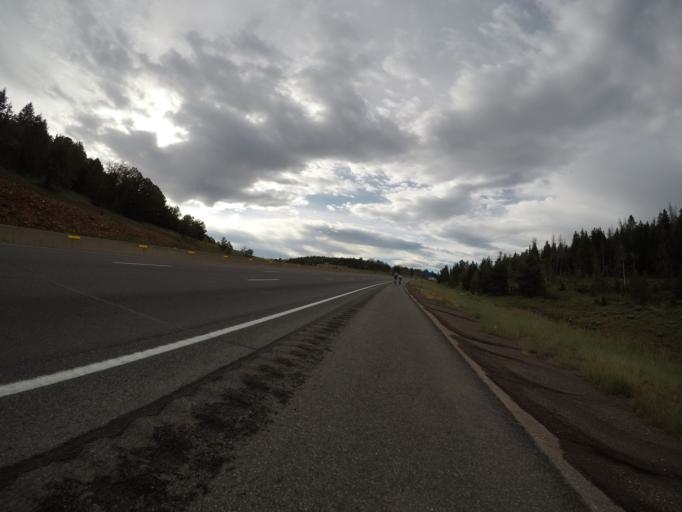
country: US
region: Wyoming
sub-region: Albany County
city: Laramie
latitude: 41.2555
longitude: -105.4490
